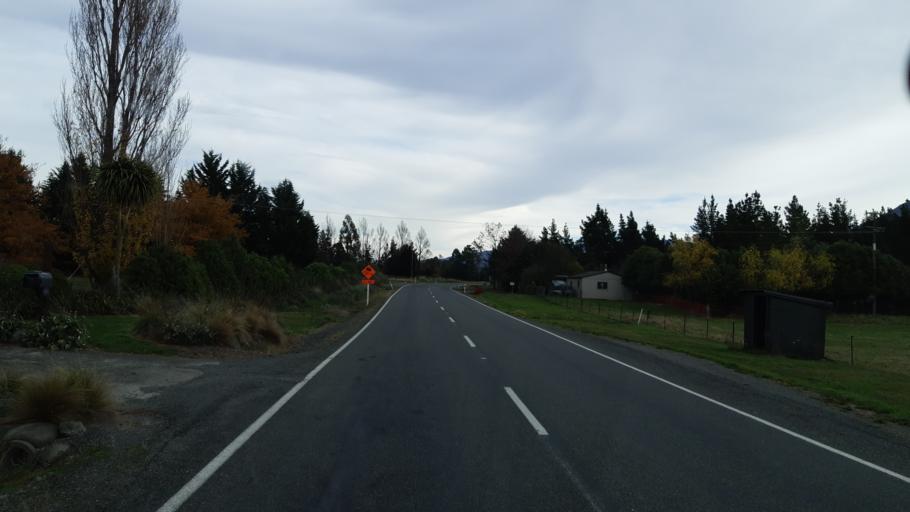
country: NZ
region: Tasman
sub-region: Tasman District
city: Brightwater
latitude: -41.6377
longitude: 173.3189
